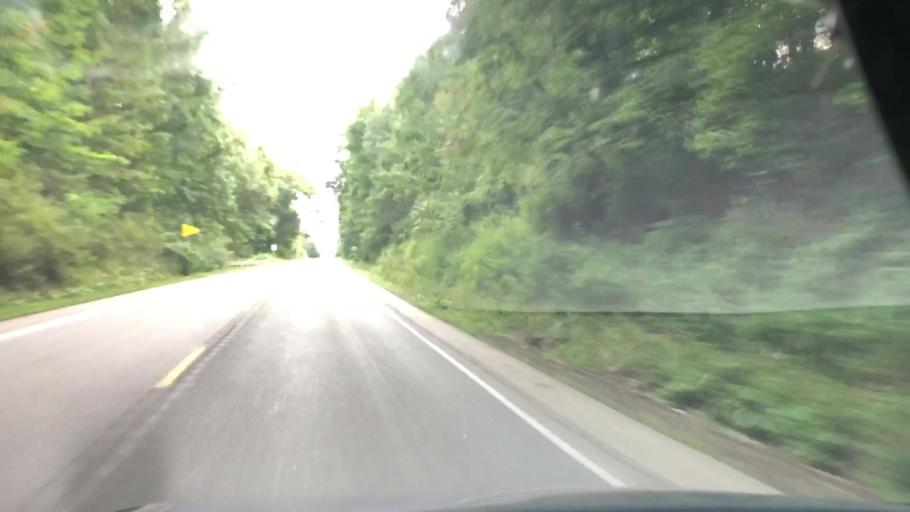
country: US
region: Pennsylvania
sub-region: Crawford County
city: Titusville
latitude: 41.6117
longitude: -79.6729
